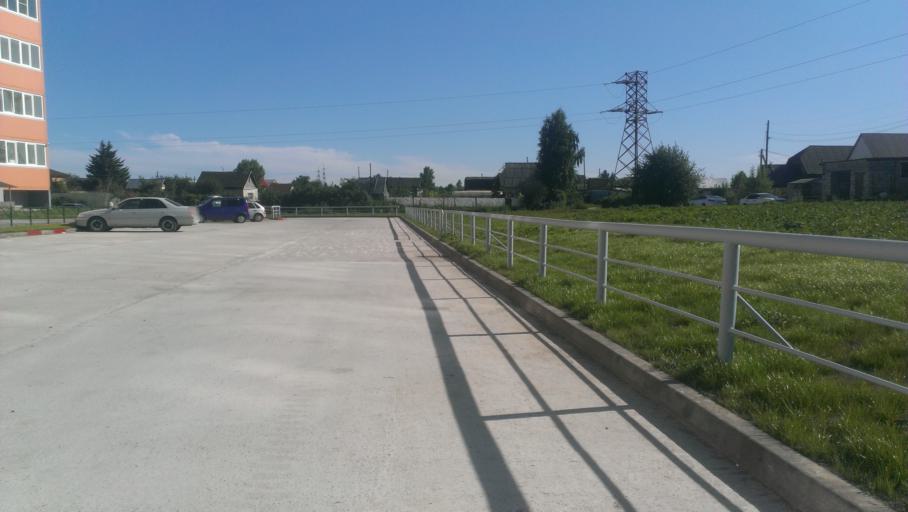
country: RU
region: Altai Krai
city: Novosilikatnyy
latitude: 53.3266
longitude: 83.6673
